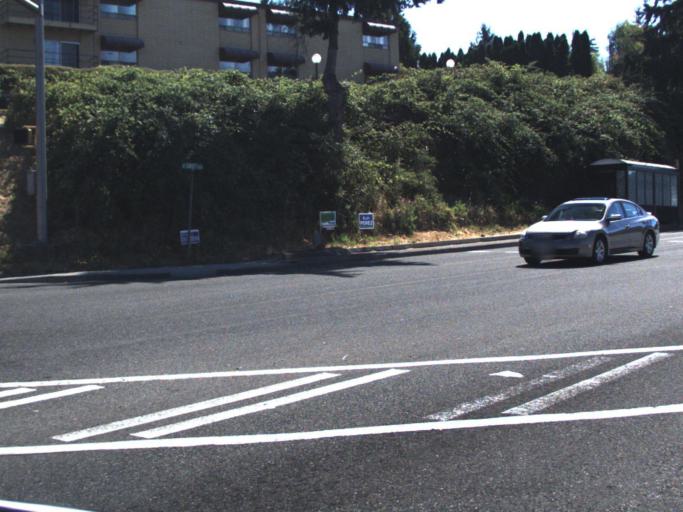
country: US
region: Washington
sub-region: King County
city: Renton
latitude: 47.5010
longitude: -122.1857
